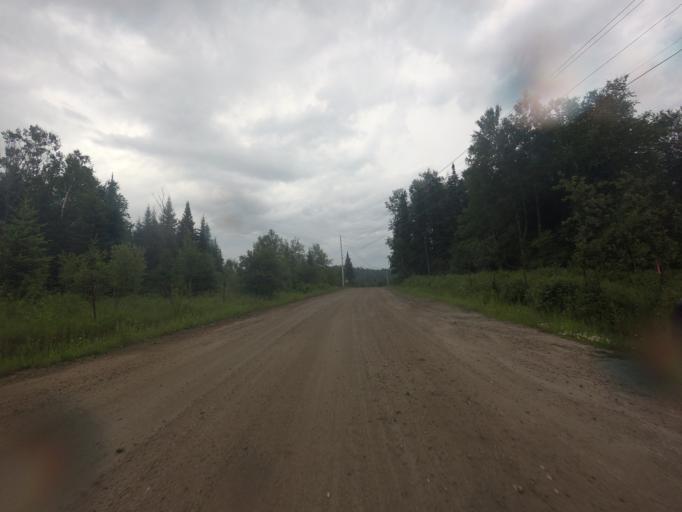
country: CA
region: Quebec
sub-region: Outaouais
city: Maniwaki
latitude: 46.4478
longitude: -75.9367
